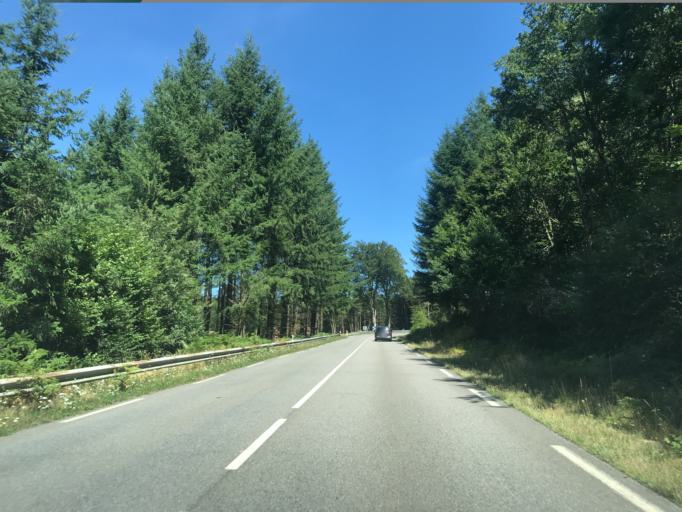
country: FR
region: Limousin
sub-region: Departement de la Correze
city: Egletons
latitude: 45.4555
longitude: 2.1144
